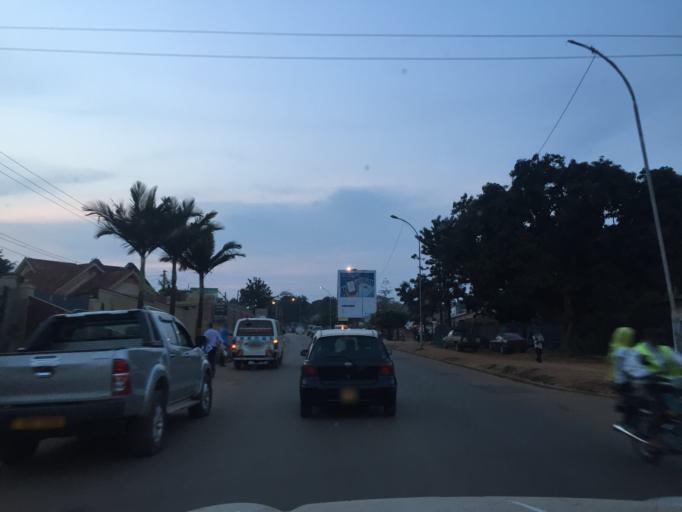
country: UG
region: Central Region
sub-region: Kampala District
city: Kampala
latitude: 0.2817
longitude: 32.6115
